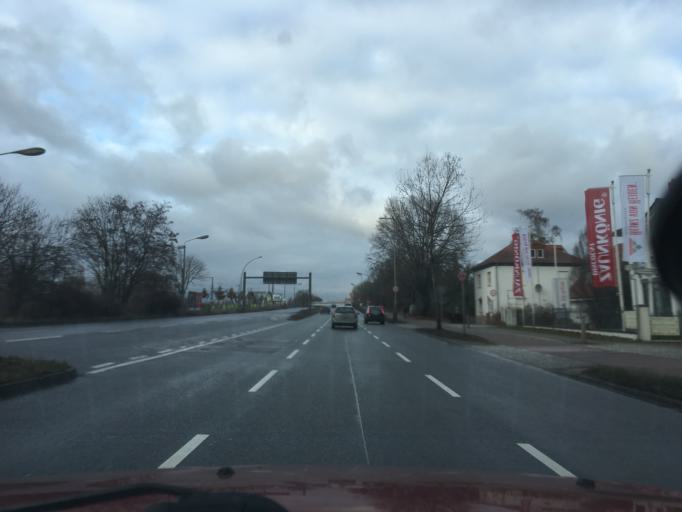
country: DE
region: Berlin
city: Adlershof
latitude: 52.4241
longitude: 13.5582
